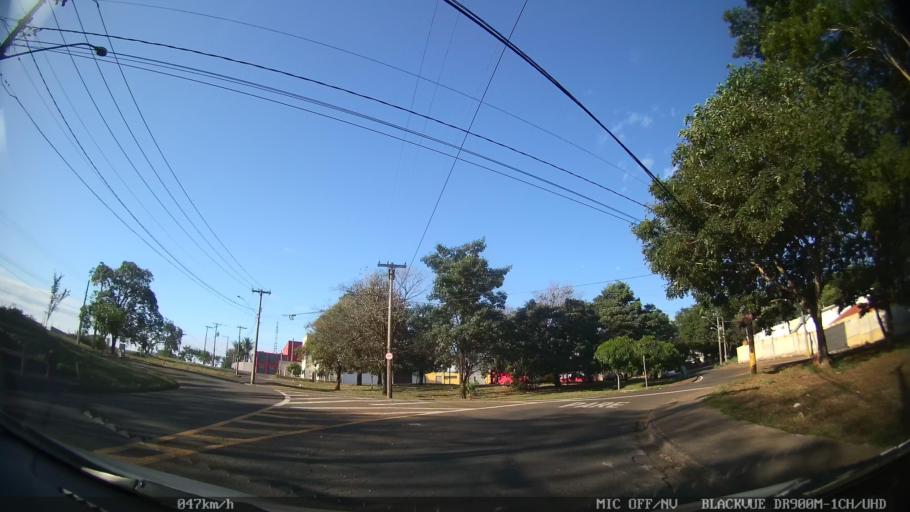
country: BR
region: Sao Paulo
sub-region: Piracicaba
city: Piracicaba
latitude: -22.6755
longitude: -47.6309
